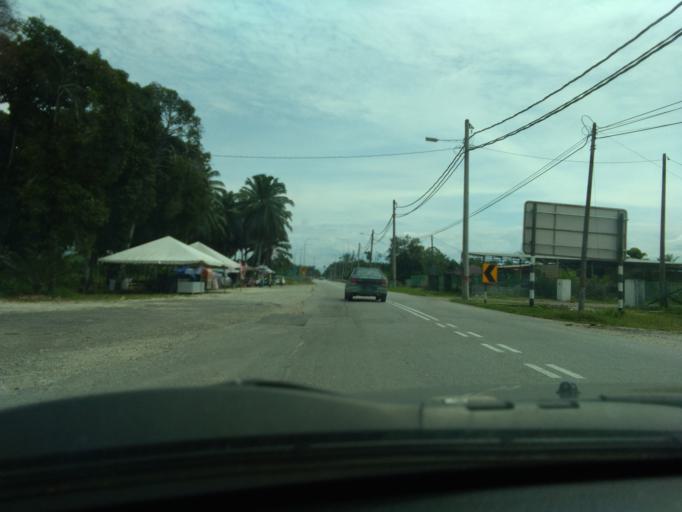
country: MY
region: Perak
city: Bagan Serai
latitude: 5.0660
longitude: 100.5961
